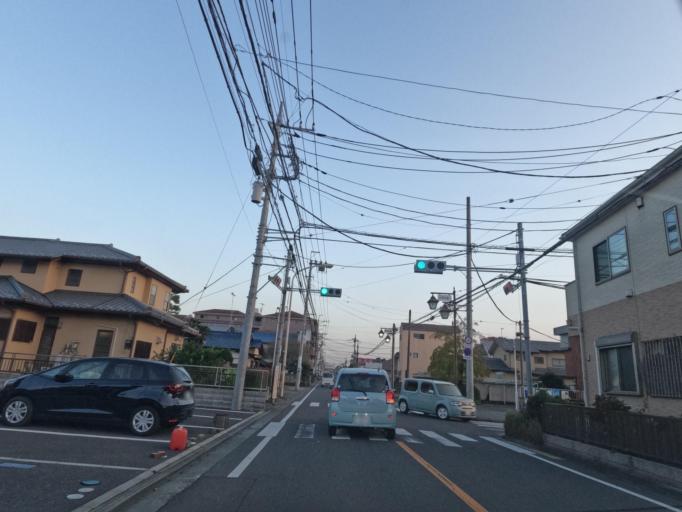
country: JP
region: Saitama
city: Ageoshimo
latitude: 35.9716
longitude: 139.6189
